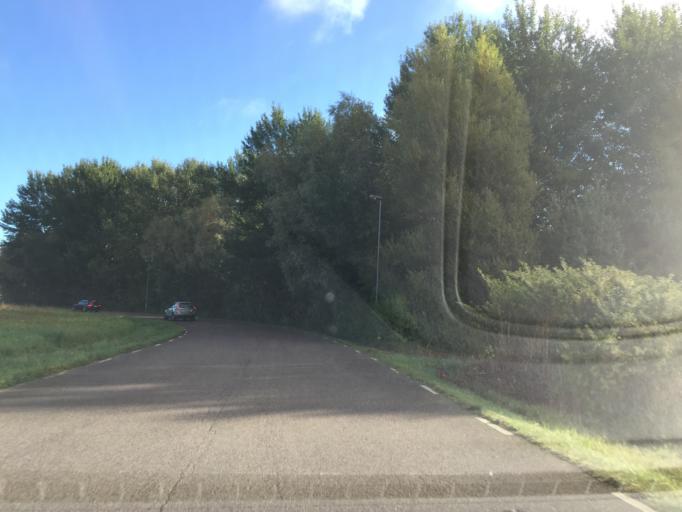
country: SE
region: Skane
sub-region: Staffanstorps Kommun
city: Staffanstorp
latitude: 55.6325
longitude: 13.2096
